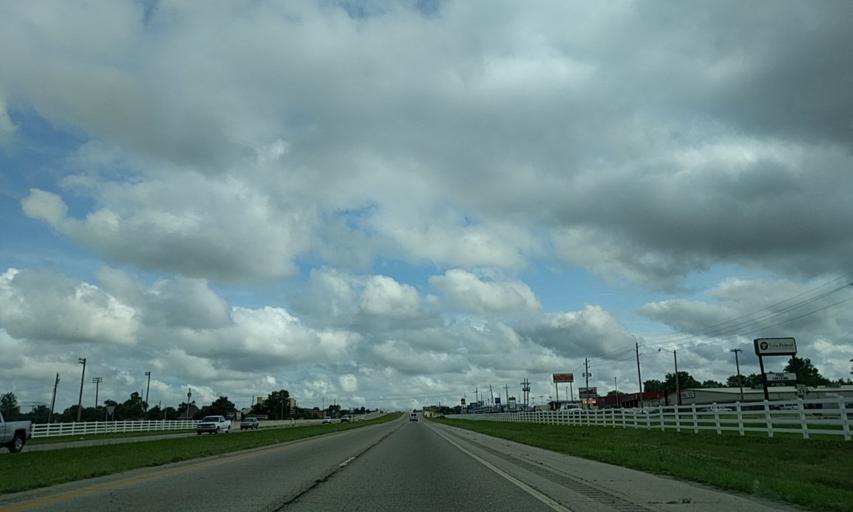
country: US
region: Oklahoma
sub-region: Tulsa County
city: Owasso
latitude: 36.2726
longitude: -95.8479
